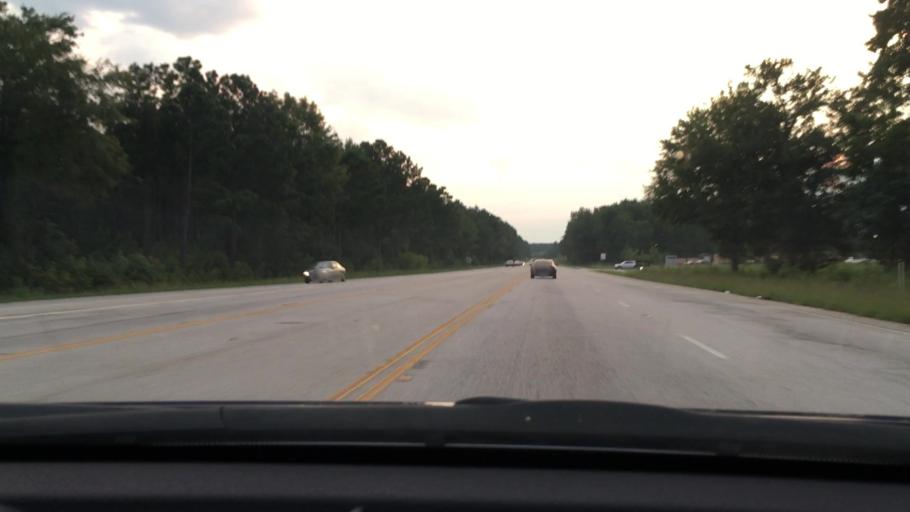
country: US
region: South Carolina
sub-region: Sumter County
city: Cherryvale
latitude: 33.9373
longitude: -80.4221
